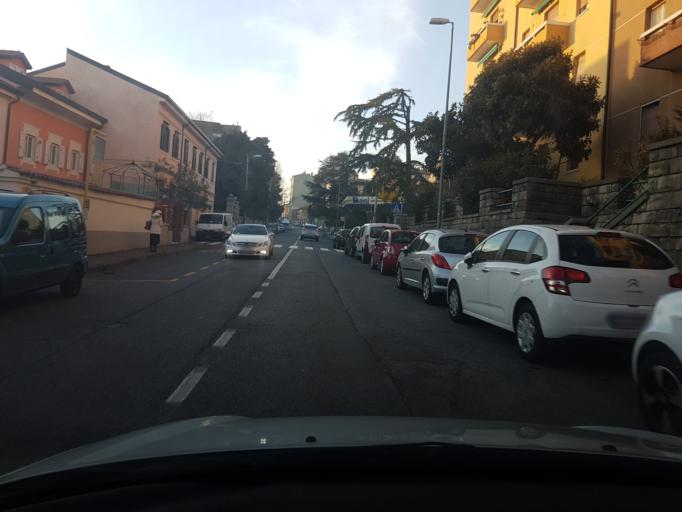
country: IT
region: Friuli Venezia Giulia
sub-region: Provincia di Trieste
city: Villa Opicina
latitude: 45.6687
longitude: 13.7650
